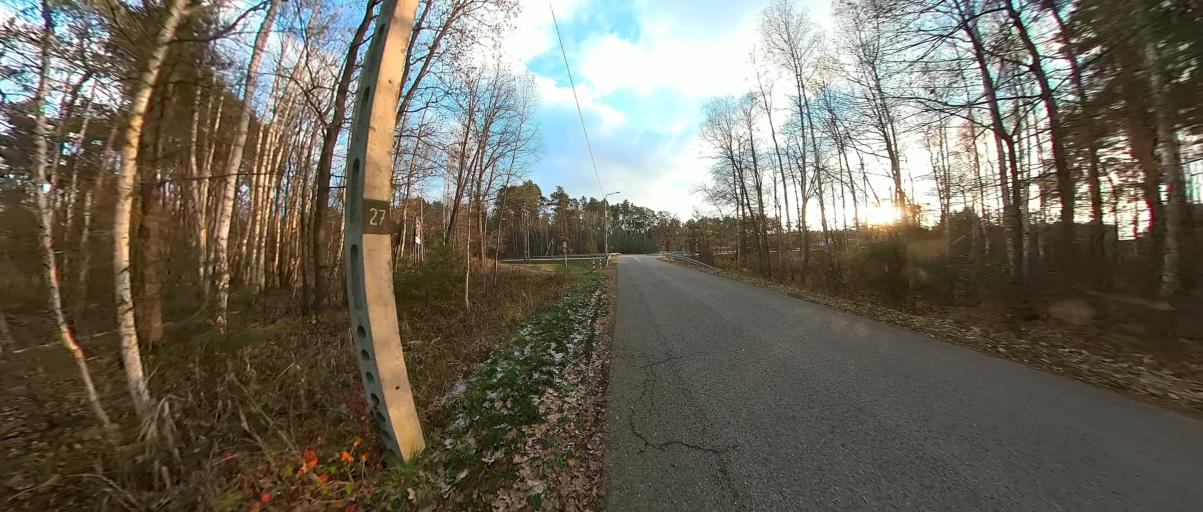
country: PL
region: Masovian Voivodeship
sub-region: Powiat bialobrzeski
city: Bialobrzegi
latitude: 51.6502
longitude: 20.9750
